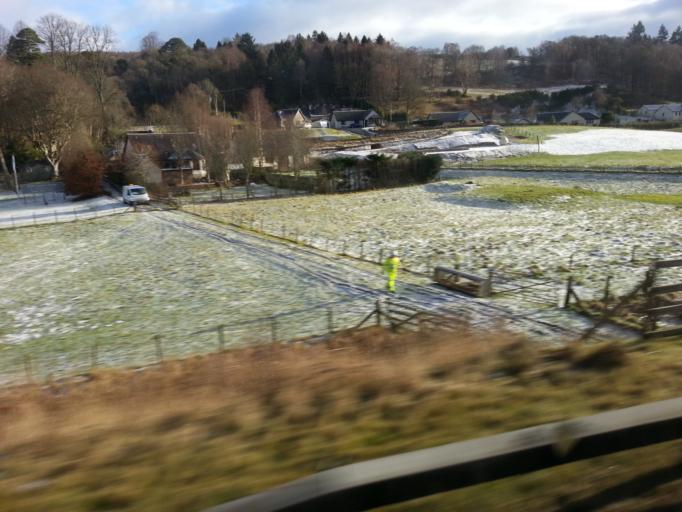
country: GB
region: Scotland
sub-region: Perth and Kinross
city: Pitlochry
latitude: 56.6858
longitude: -3.7014
